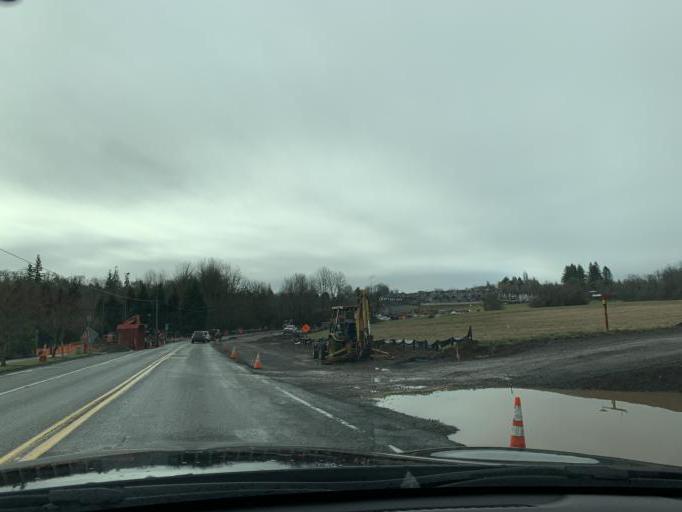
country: US
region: Washington
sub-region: Clark County
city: Camas
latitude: 45.5980
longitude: -122.4505
